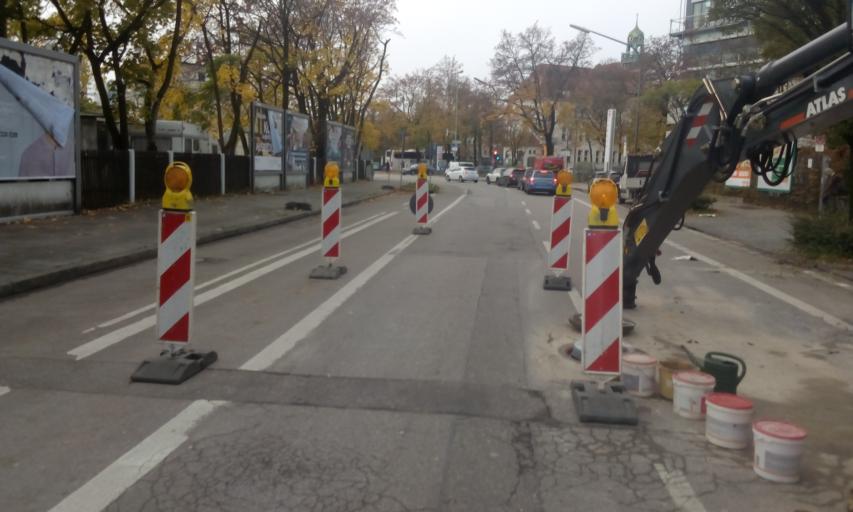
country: DE
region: Bavaria
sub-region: Upper Bavaria
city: Munich
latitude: 48.1468
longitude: 11.5509
